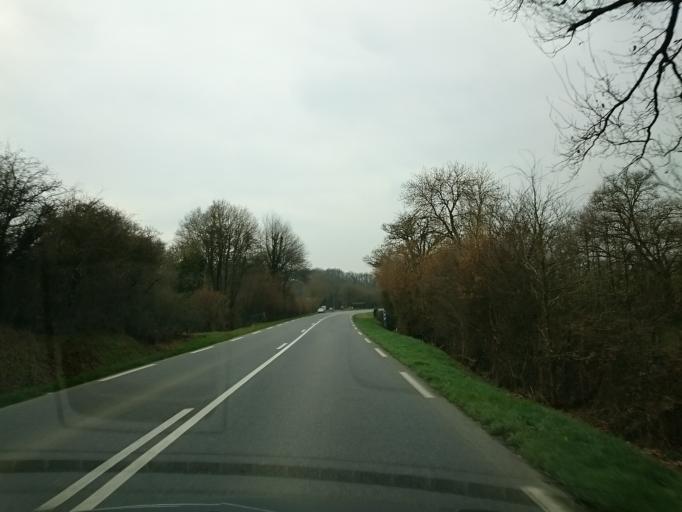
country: FR
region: Brittany
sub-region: Departement d'Ille-et-Vilaine
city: Pance
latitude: 47.8790
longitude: -1.6420
